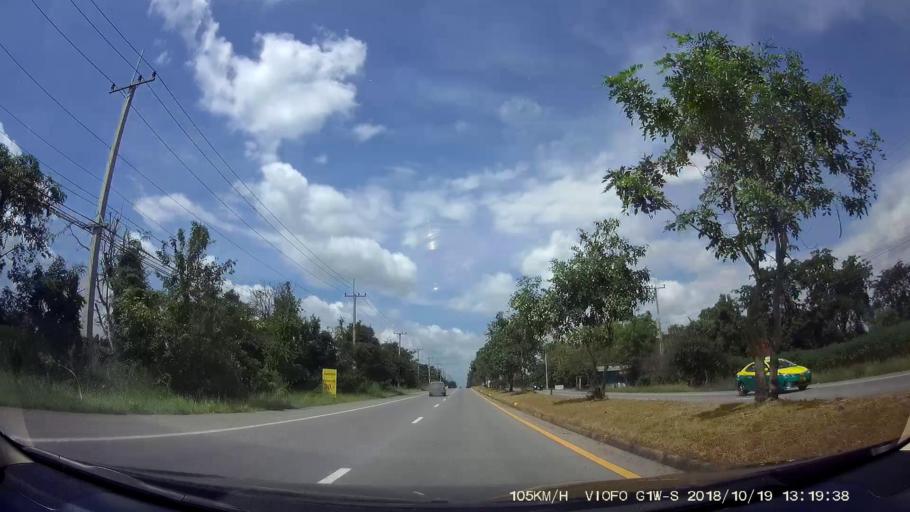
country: TH
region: Chaiyaphum
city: Chatturat
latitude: 15.4328
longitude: 101.8306
